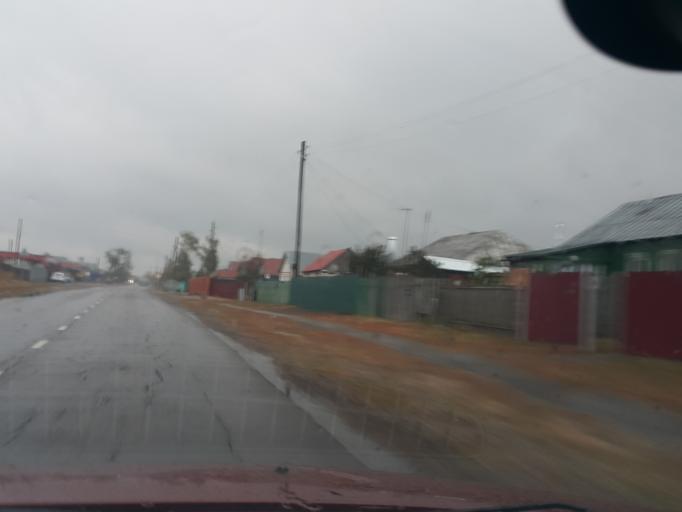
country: RU
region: Tambov
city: Kotovsk
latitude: 52.5401
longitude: 41.4778
